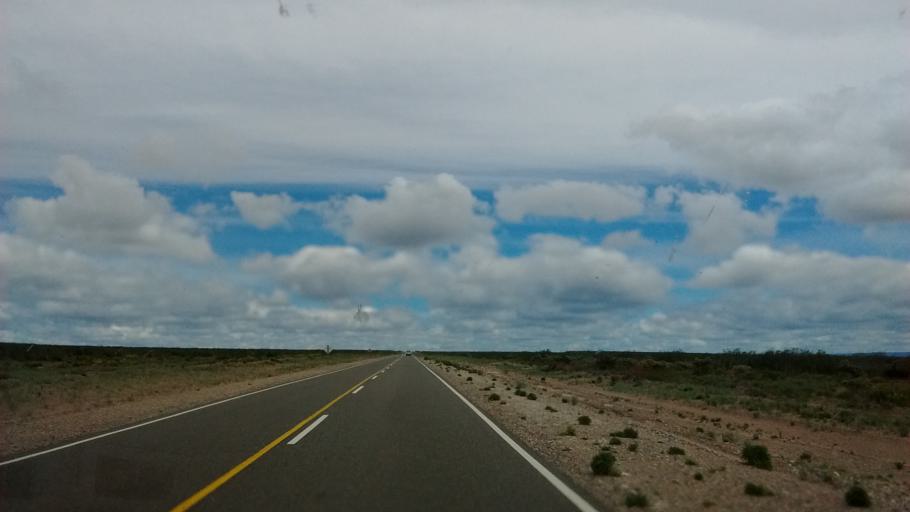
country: AR
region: Neuquen
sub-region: Departamento de Picun Leufu
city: Picun Leufu
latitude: -39.7487
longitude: -69.6197
